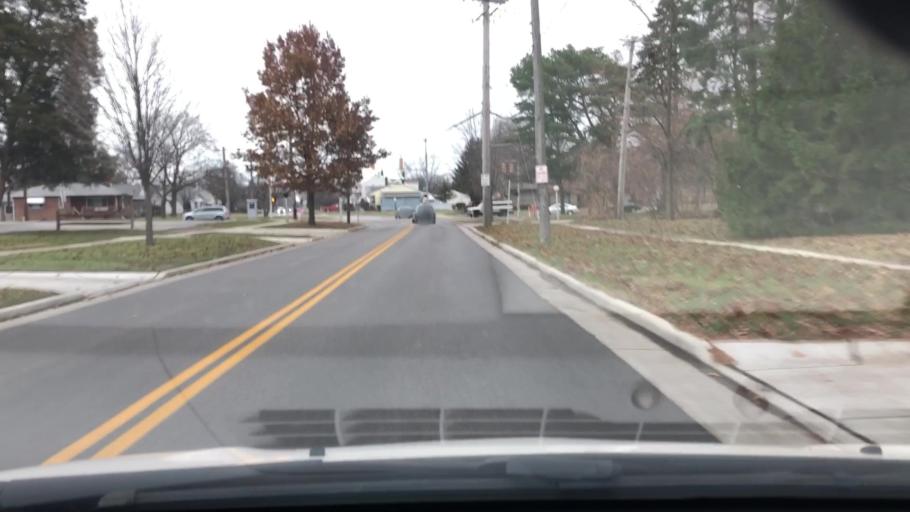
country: US
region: Ohio
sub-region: Lucas County
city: Maumee
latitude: 41.5712
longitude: -83.6456
